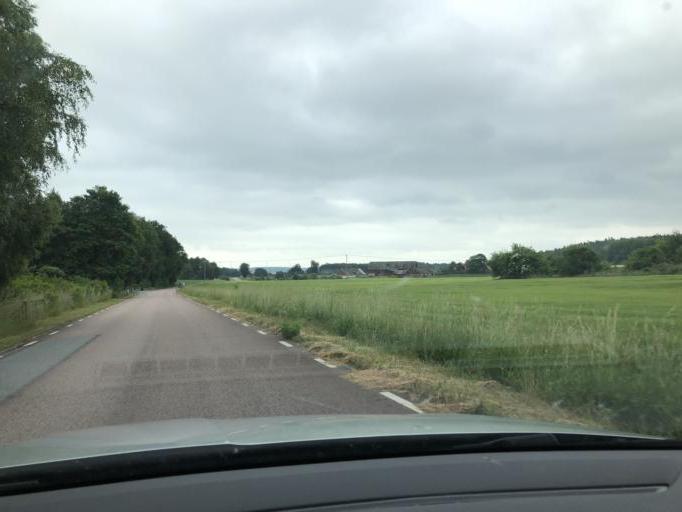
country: SE
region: Blekinge
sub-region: Solvesborgs Kommun
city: Soelvesborg
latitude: 56.1279
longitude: 14.6077
